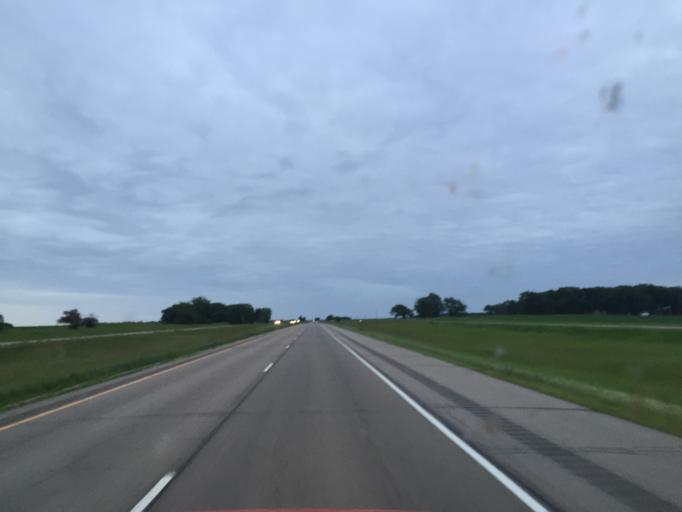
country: US
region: Minnesota
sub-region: Mower County
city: Austin
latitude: 43.6589
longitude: -93.0844
